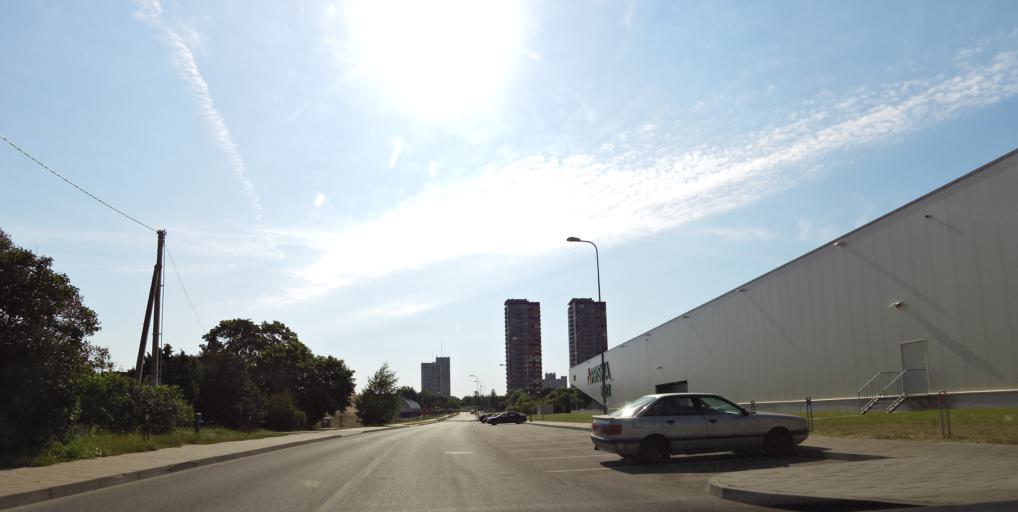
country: LT
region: Vilnius County
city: Justiniskes
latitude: 54.7031
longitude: 25.2120
